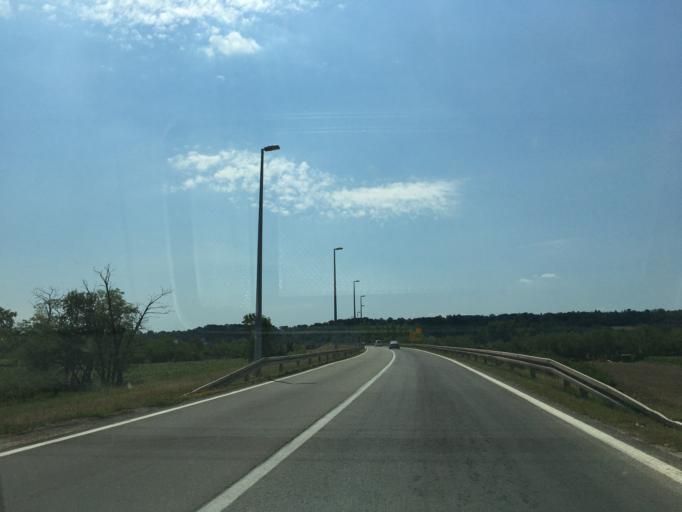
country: RS
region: Central Serbia
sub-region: Podunavski Okrug
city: Smederevo
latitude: 44.5893
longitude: 20.9576
